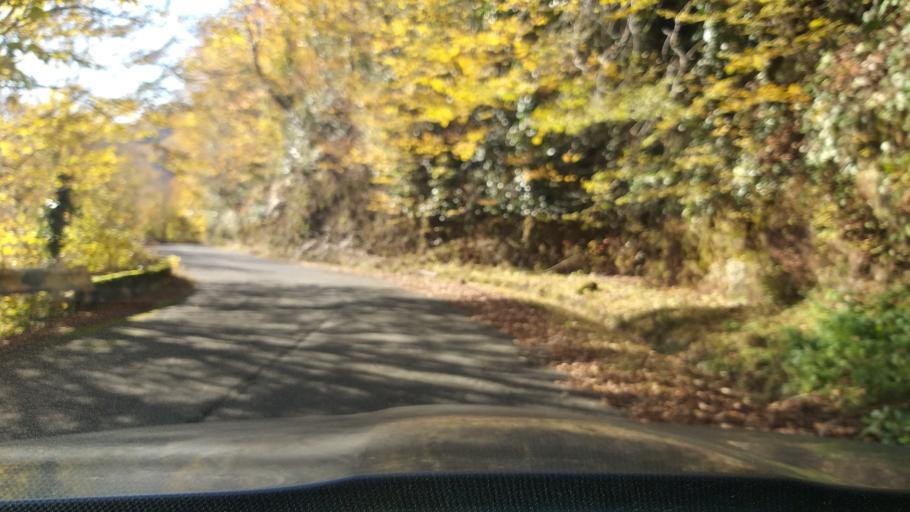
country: GE
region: Abkhazia
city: Bich'vinta
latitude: 43.1925
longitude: 40.4558
